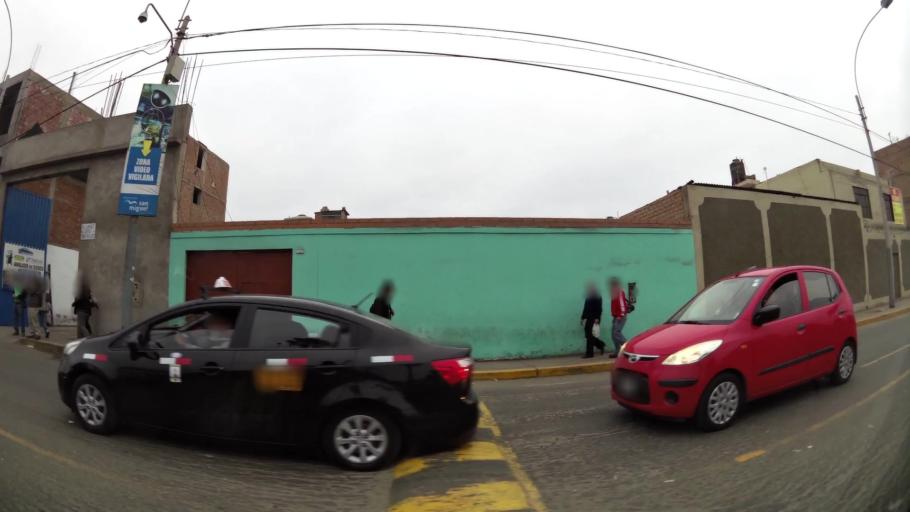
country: PE
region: Callao
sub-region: Callao
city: Callao
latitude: -12.0774
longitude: -77.1104
